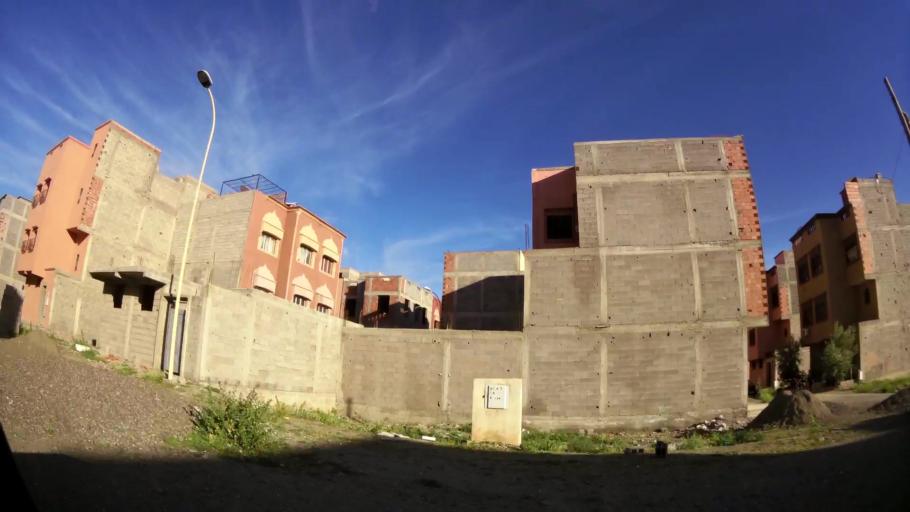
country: MA
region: Marrakech-Tensift-Al Haouz
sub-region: Marrakech
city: Marrakesh
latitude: 31.7610
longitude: -8.0999
